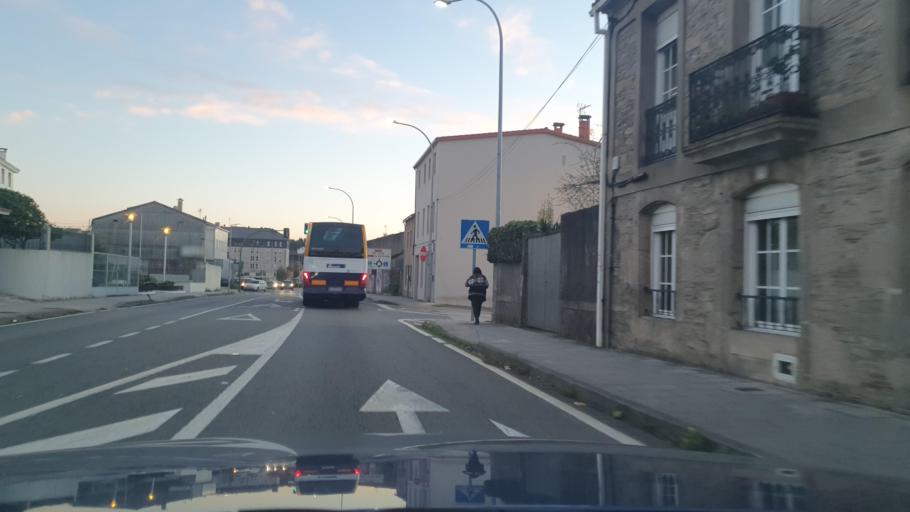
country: ES
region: Galicia
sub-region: Provincia da Coruna
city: Santiago de Compostela
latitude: 42.8577
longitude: -8.5401
